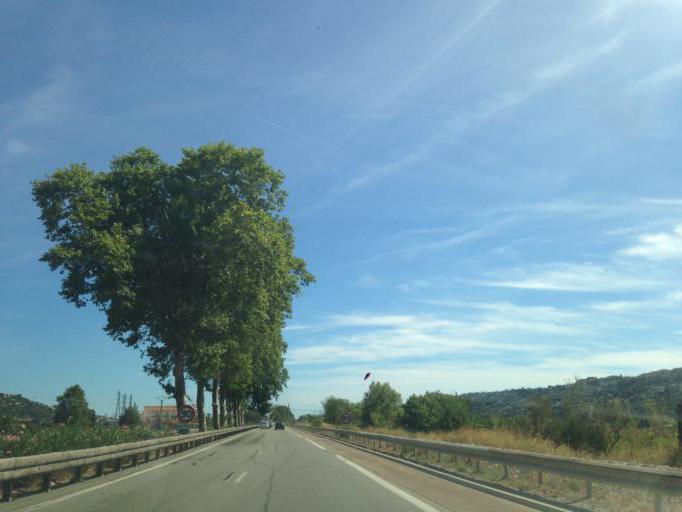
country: FR
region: Provence-Alpes-Cote d'Azur
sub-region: Departement des Alpes-Maritimes
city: Gattieres
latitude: 43.7266
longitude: 7.1854
